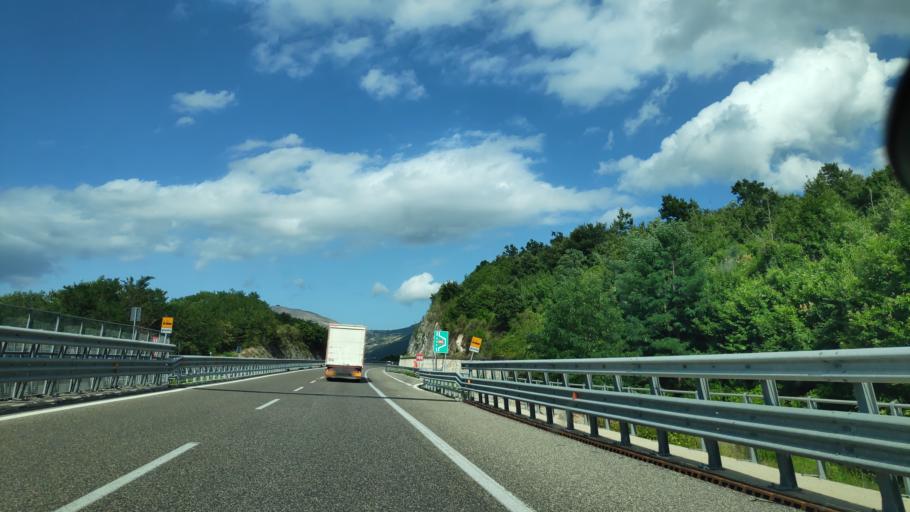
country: IT
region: Campania
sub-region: Provincia di Salerno
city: Pertosa
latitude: 40.5307
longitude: 15.4378
